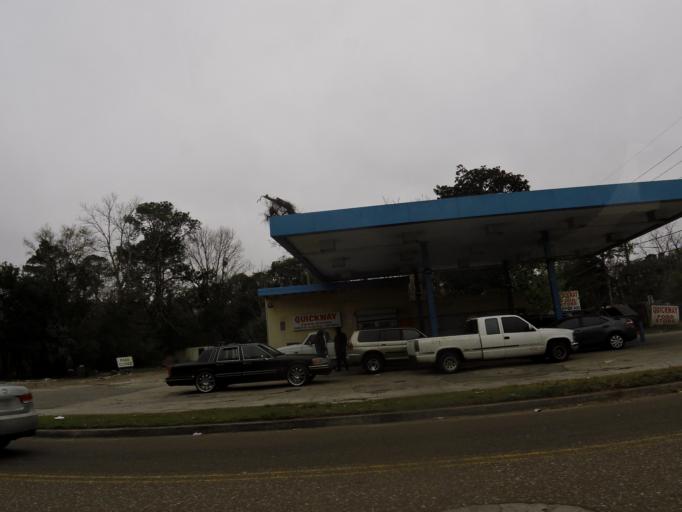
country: US
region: Florida
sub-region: Duval County
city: Jacksonville
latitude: 30.3712
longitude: -81.6990
